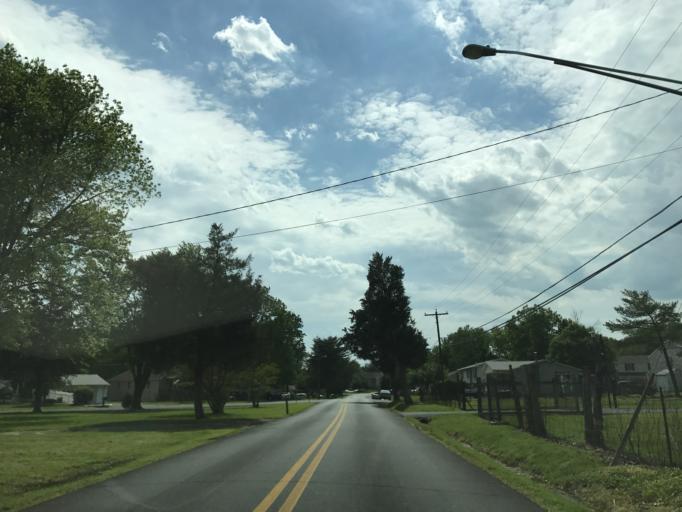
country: US
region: Maryland
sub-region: Baltimore County
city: Bowleys Quarters
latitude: 39.3723
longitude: -76.3490
